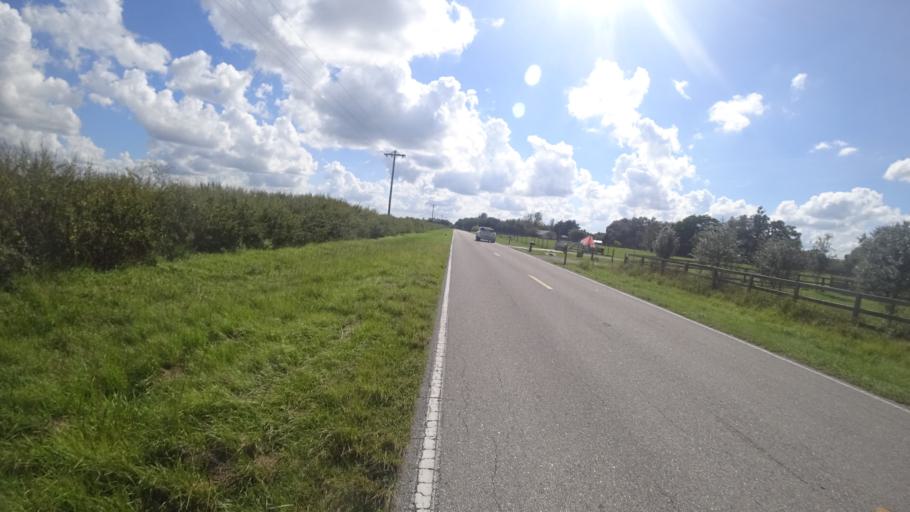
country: US
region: Florida
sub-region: Sarasota County
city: Lake Sarasota
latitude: 27.3726
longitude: -82.1408
